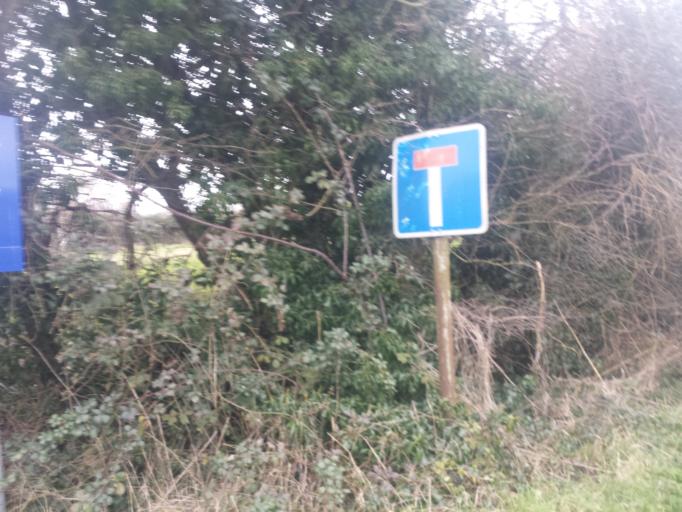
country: GB
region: England
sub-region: Essex
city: Little Clacton
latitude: 51.8796
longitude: 1.1679
